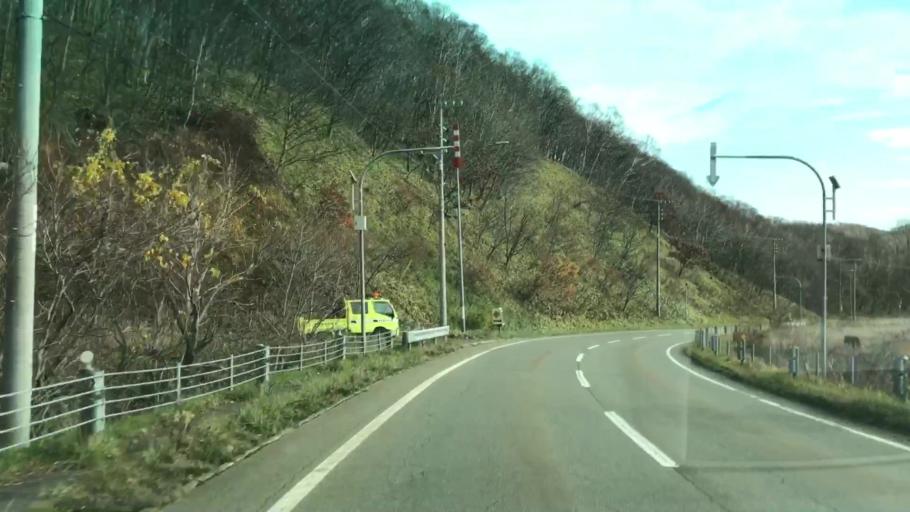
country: JP
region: Hokkaido
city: Obihiro
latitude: 42.0288
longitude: 143.2293
